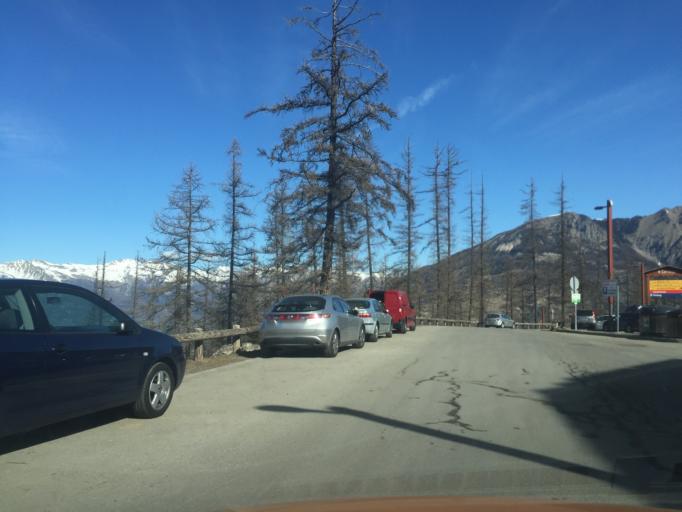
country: FR
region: Provence-Alpes-Cote d'Azur
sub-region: Departement des Hautes-Alpes
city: Embrun
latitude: 44.4852
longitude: 6.5525
